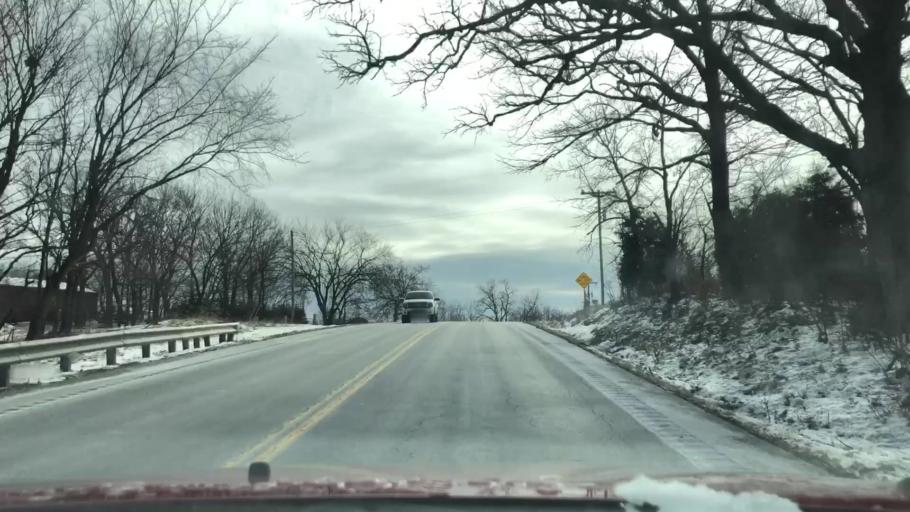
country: US
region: Missouri
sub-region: Jackson County
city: Oak Grove
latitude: 38.9345
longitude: -94.1332
